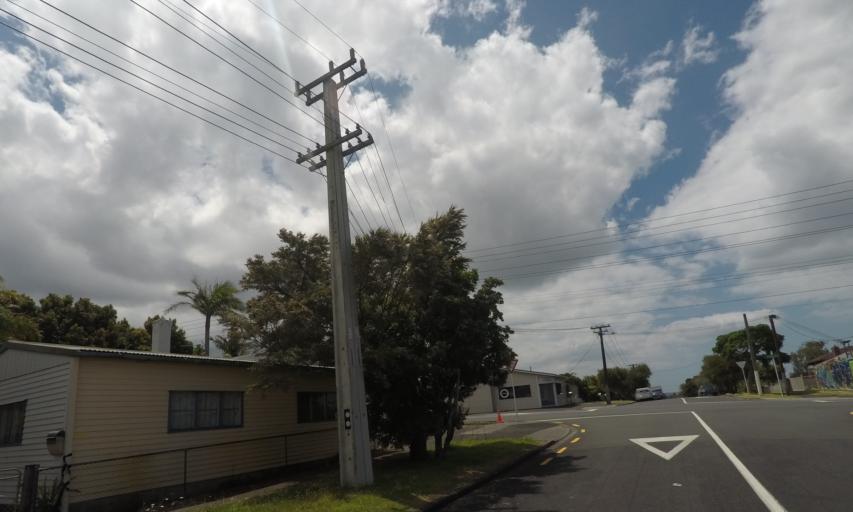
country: NZ
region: Auckland
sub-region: Auckland
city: Waitakere
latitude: -36.9049
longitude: 174.6718
